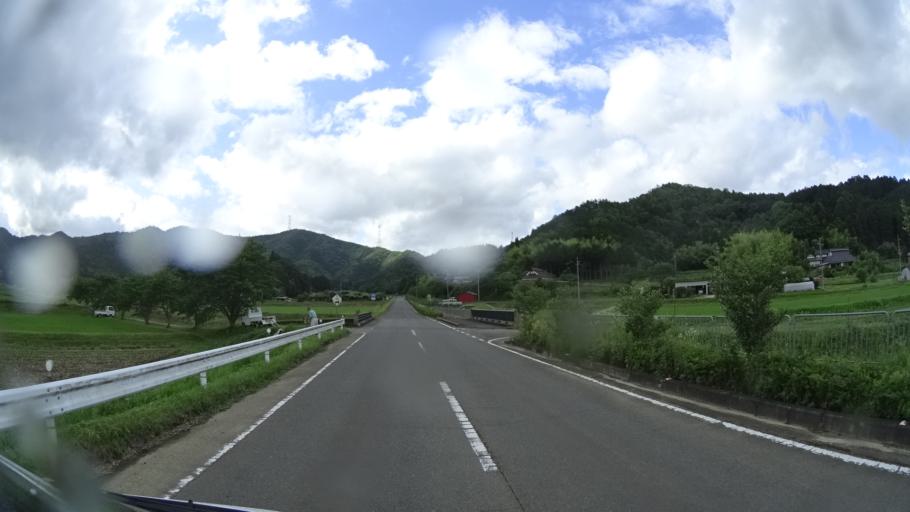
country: JP
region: Kyoto
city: Ayabe
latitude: 35.3467
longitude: 135.1990
